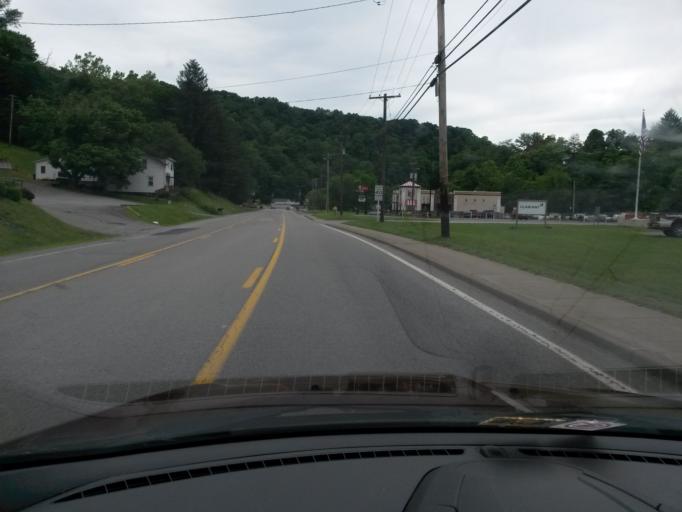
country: US
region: West Virginia
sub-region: Lewis County
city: Weston
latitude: 39.0367
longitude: -80.4533
